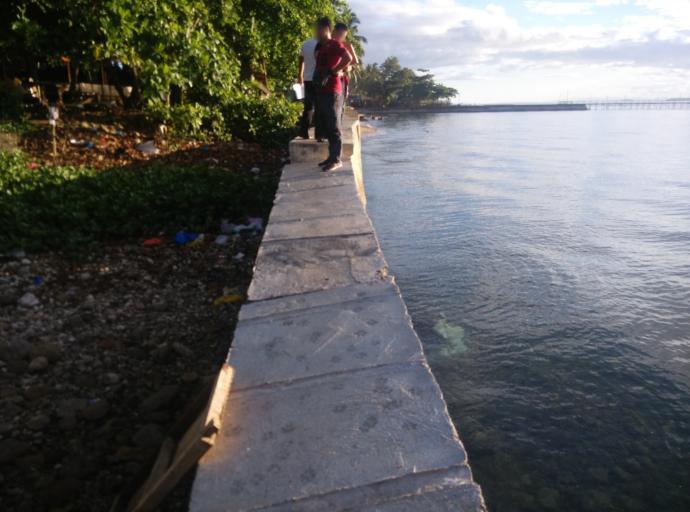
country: PH
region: Eastern Visayas
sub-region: Province of Leyte
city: Matalom
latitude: 10.2828
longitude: 124.7848
